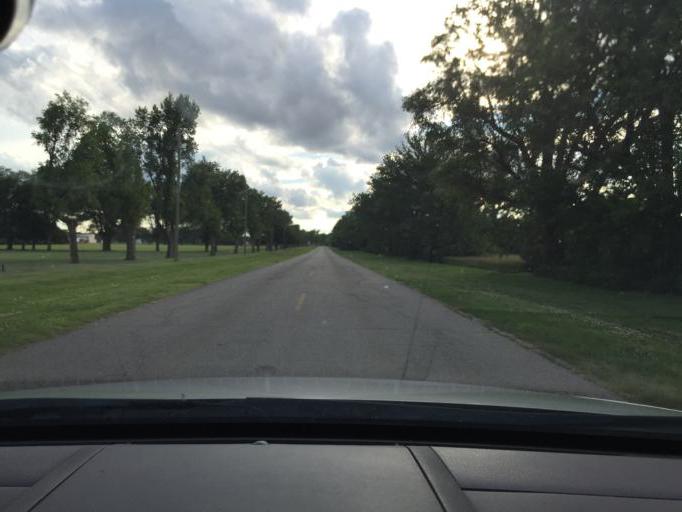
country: US
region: Kansas
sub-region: Reno County
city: Haven
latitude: 37.9264
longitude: -97.8876
